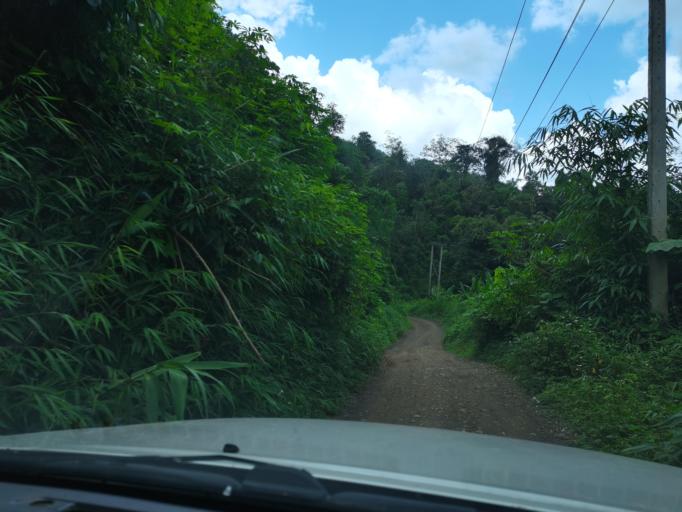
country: LA
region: Loungnamtha
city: Muang Long
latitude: 20.7676
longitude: 101.0176
